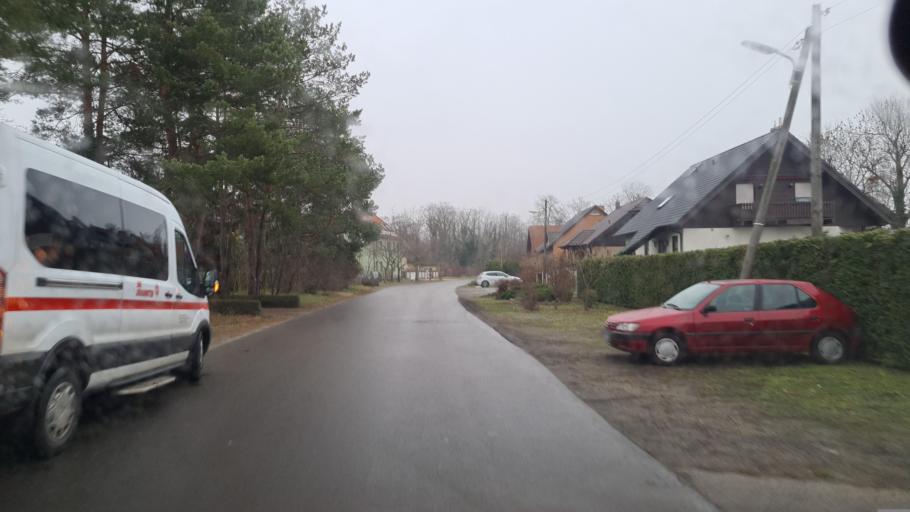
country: DE
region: Brandenburg
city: Cottbus
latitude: 51.7467
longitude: 14.2969
